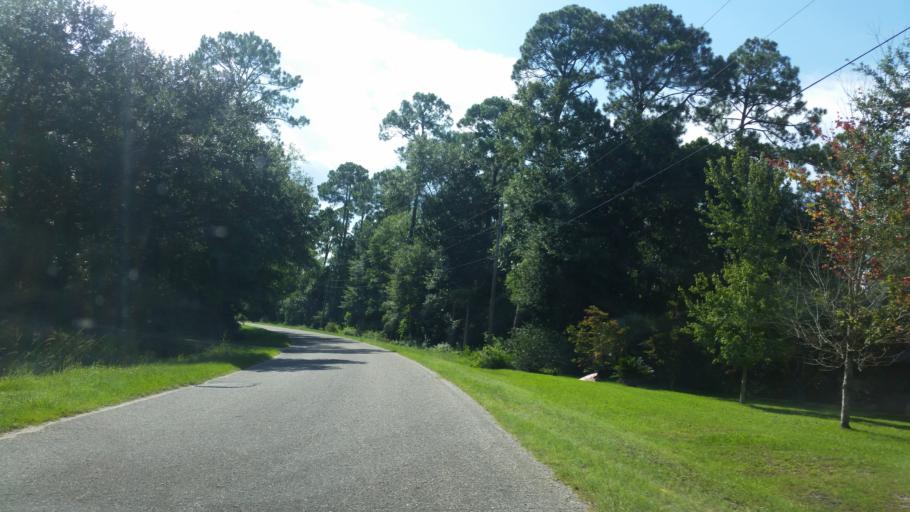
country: US
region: Florida
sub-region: Santa Rosa County
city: Pace
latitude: 30.5814
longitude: -87.1548
